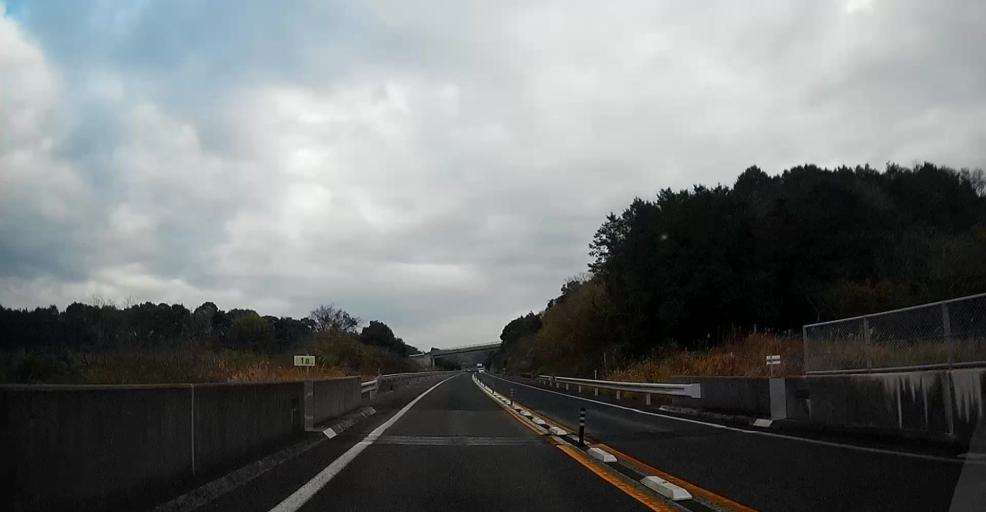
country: JP
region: Kumamoto
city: Hondo
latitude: 32.5098
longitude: 130.3236
